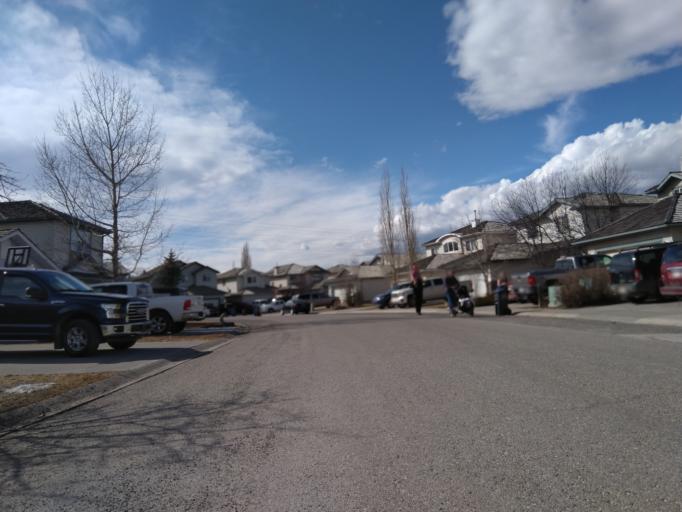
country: CA
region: Alberta
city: Cochrane
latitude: 51.1882
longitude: -114.5115
